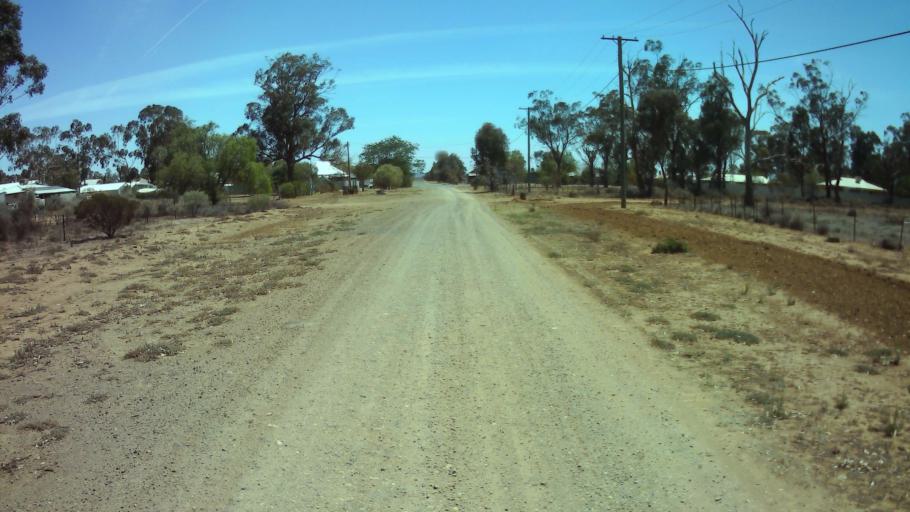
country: AU
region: New South Wales
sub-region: Weddin
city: Grenfell
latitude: -33.8456
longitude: 147.7387
